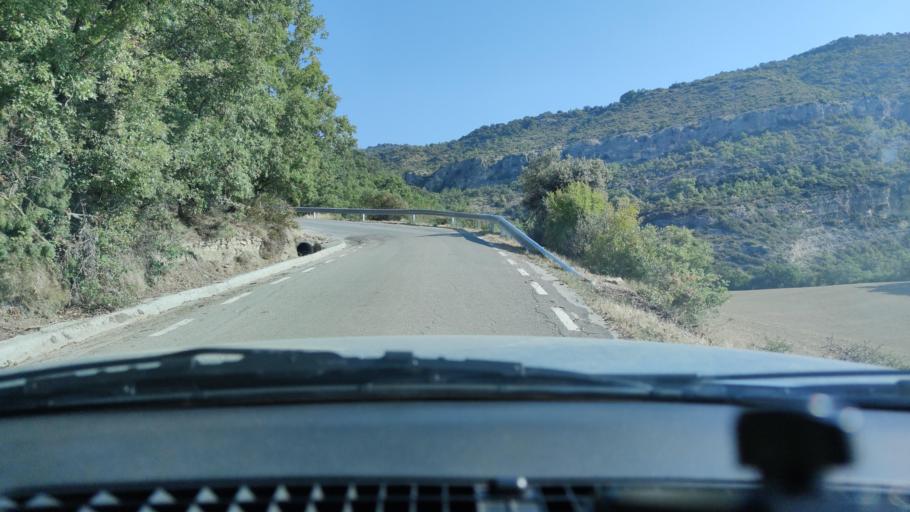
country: ES
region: Catalonia
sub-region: Provincia de Lleida
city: Llimiana
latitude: 42.0835
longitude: 0.8430
